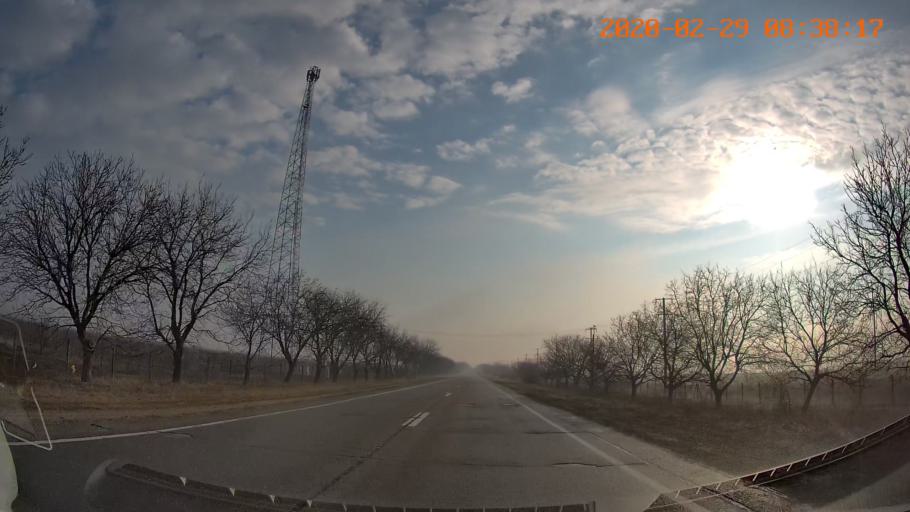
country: MD
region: Anenii Noi
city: Varnita
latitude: 46.9217
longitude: 29.3753
